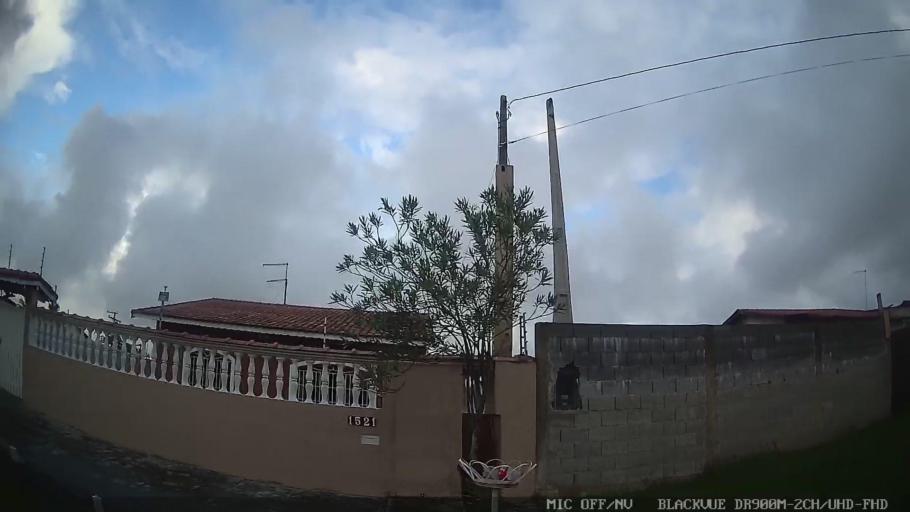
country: BR
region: Sao Paulo
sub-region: Itanhaem
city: Itanhaem
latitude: -24.2061
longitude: -46.8415
